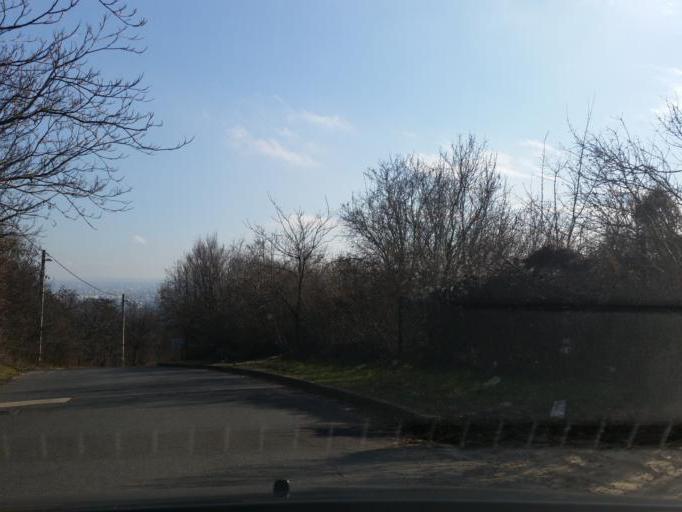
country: HU
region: Budapest
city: Budapest II. keruelet
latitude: 47.5331
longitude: 19.0133
